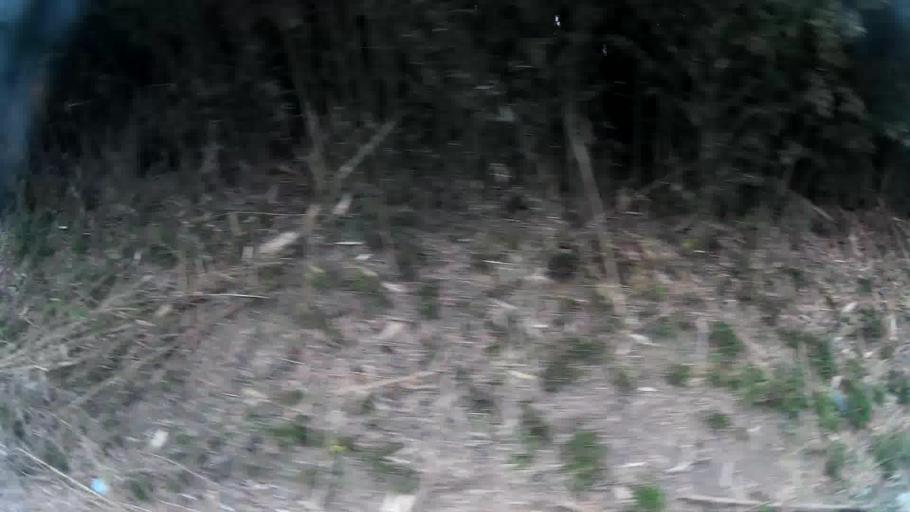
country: CO
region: Risaralda
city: La Virginia
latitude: 4.8346
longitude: -75.8516
